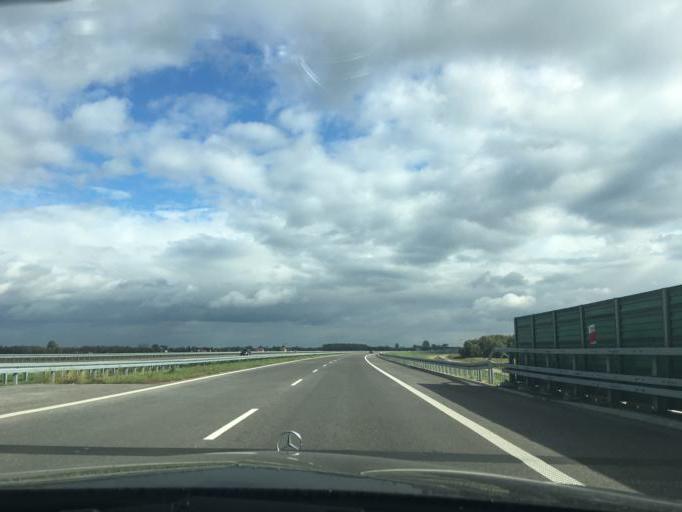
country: PL
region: Subcarpathian Voivodeship
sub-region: Powiat rzeszowski
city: Wolka Podlesna
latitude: 50.0958
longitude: 22.1164
